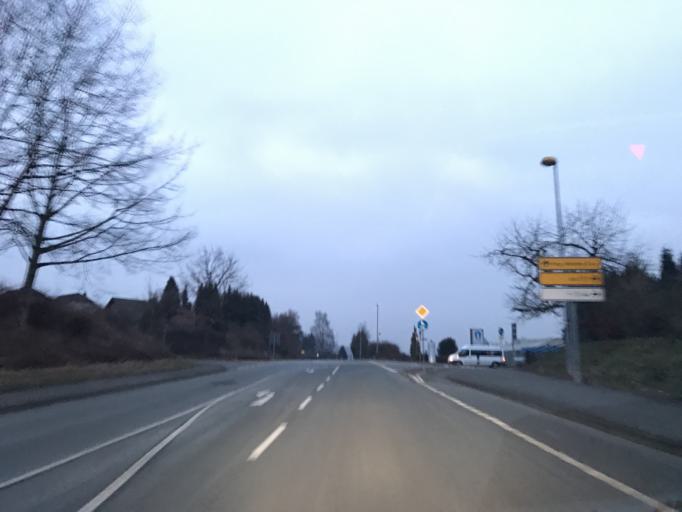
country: DE
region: Hesse
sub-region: Regierungsbezirk Kassel
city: Hofgeismar
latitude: 51.5015
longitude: 9.3829
